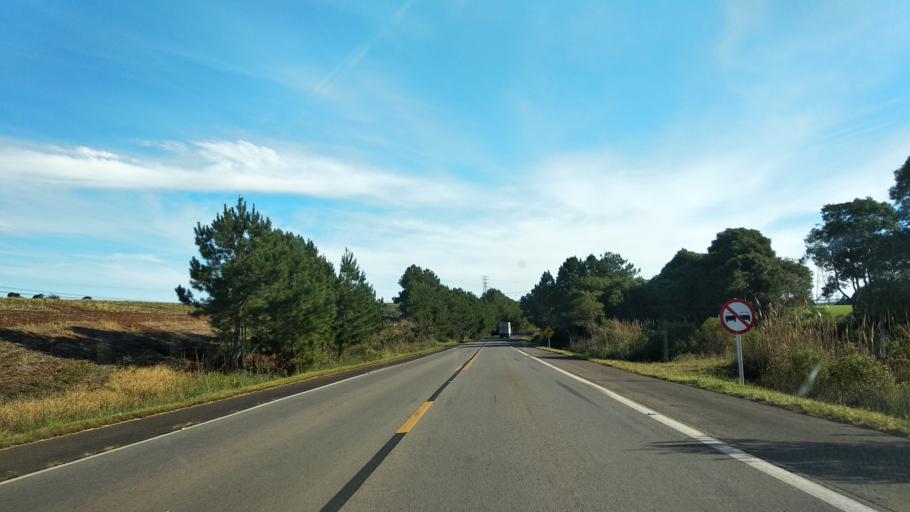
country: BR
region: Santa Catarina
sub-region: Celso Ramos
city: Celso Ramos
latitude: -27.5361
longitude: -51.4036
